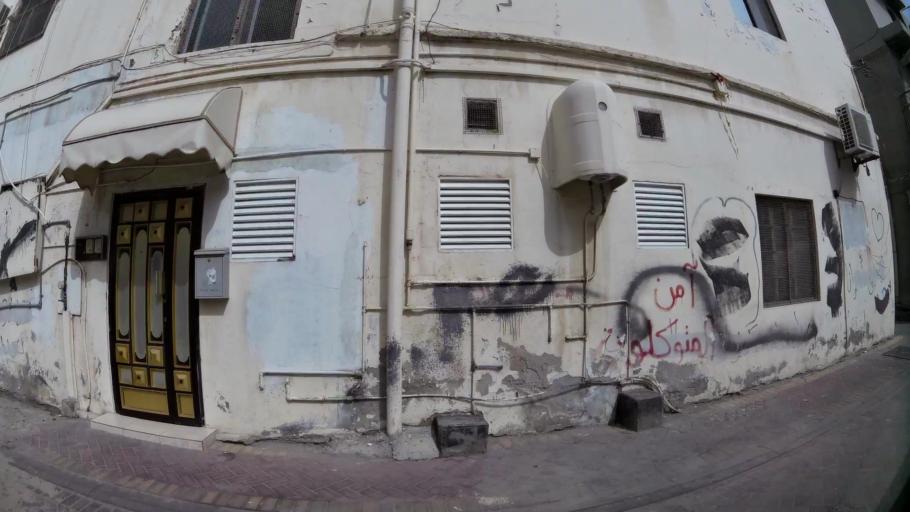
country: BH
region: Manama
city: Jidd Hafs
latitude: 26.2310
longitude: 50.5286
